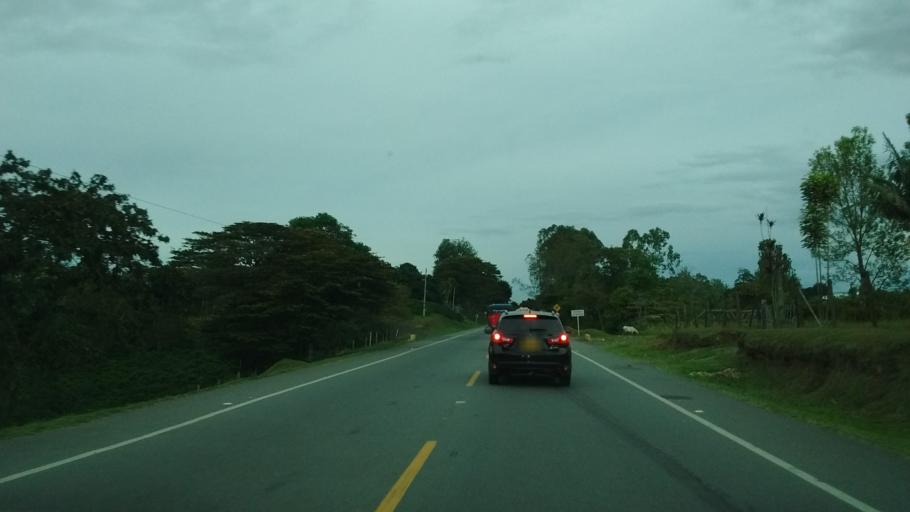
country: CO
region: Cauca
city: Morales
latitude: 2.7526
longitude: -76.5527
